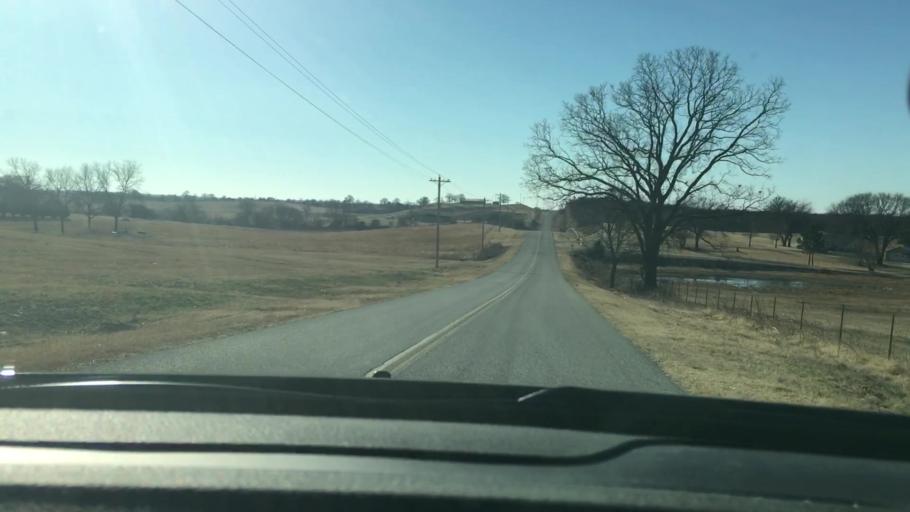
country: US
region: Oklahoma
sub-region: Love County
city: Marietta
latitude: 33.9365
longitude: -97.3522
